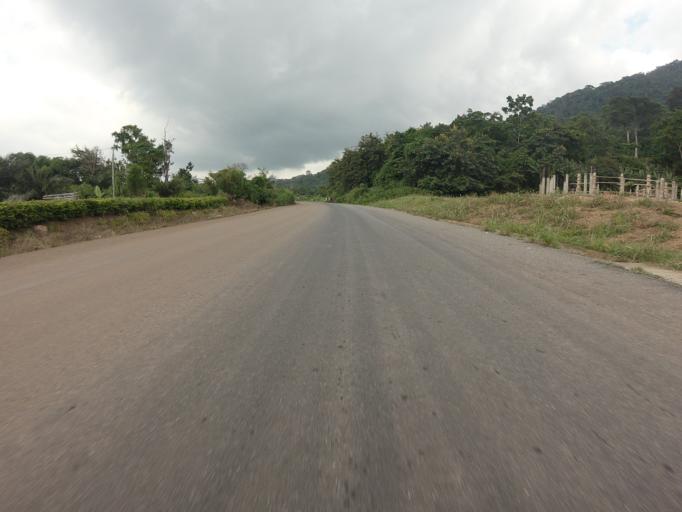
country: GH
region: Volta
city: Kpandu
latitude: 6.9136
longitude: 0.4526
